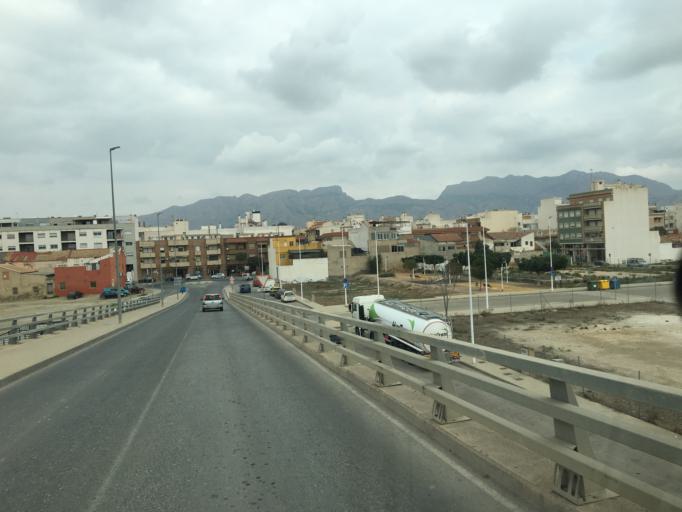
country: ES
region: Murcia
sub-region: Murcia
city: Beniel
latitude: 38.0467
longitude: -0.9974
